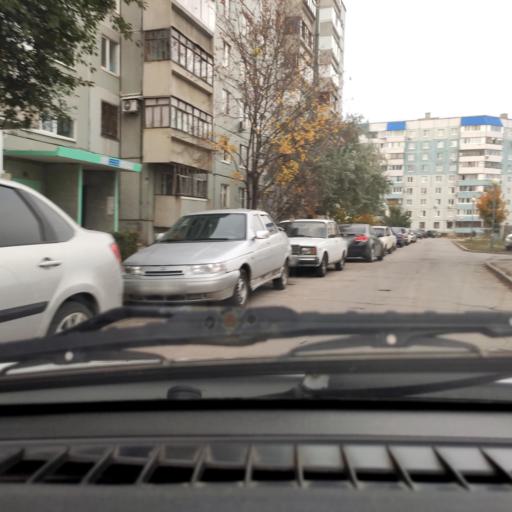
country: RU
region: Samara
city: Tol'yatti
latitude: 53.5417
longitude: 49.3541
